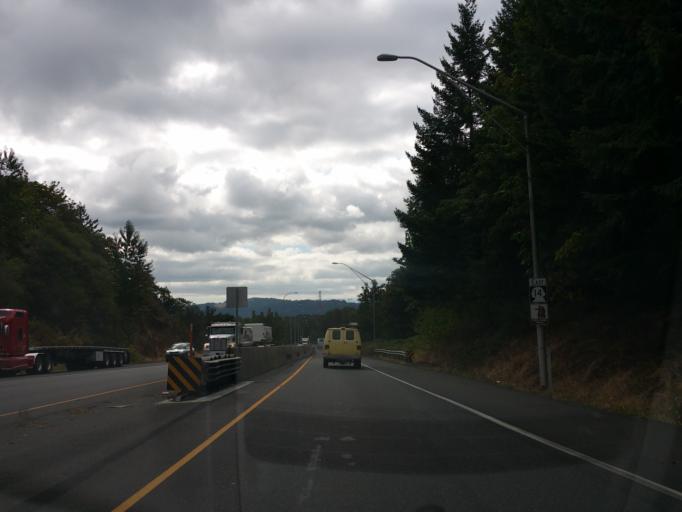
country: US
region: Washington
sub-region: Clark County
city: Camas
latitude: 45.5795
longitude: -122.4257
